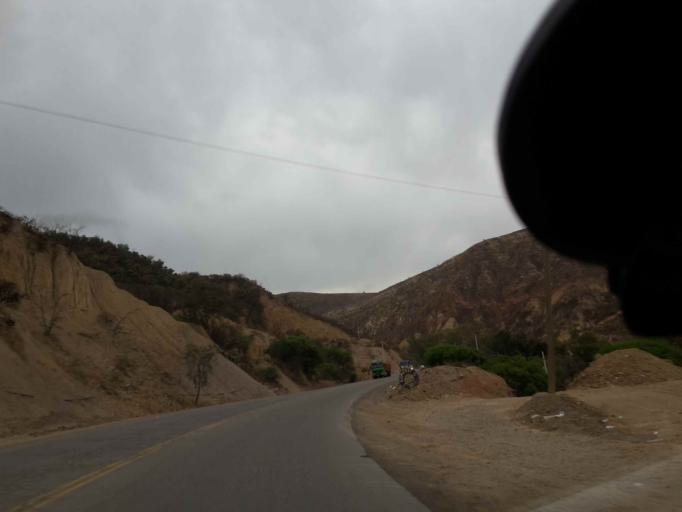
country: BO
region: Cochabamba
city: Sipe Sipe
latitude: -17.5462
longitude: -66.3408
